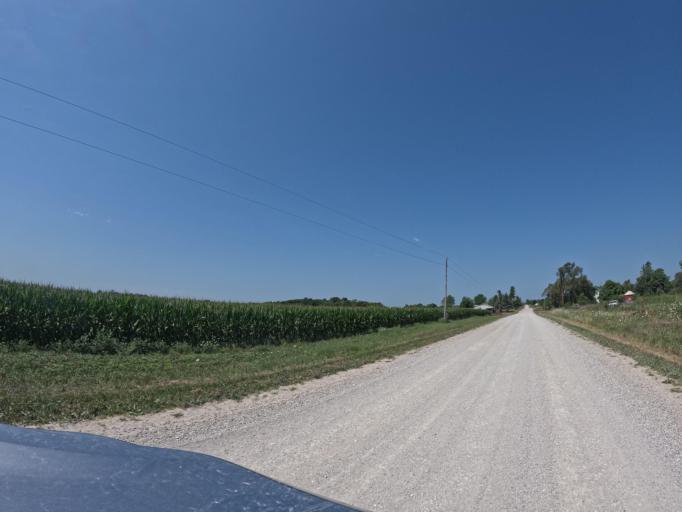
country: US
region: Iowa
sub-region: Henry County
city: Mount Pleasant
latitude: 40.8892
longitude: -91.5806
